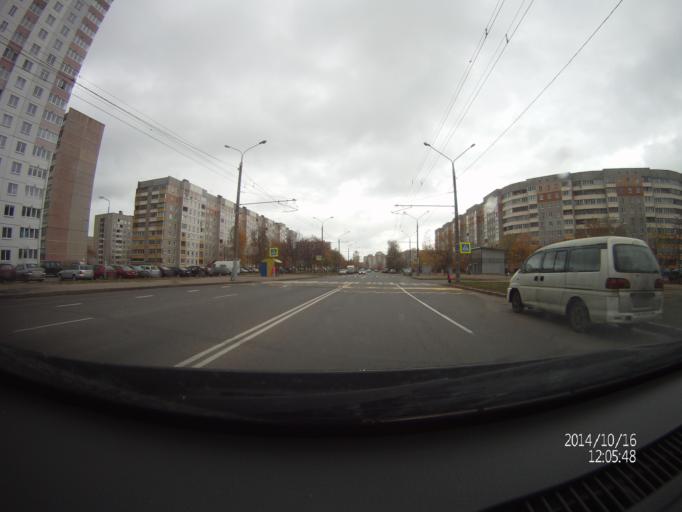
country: BY
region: Minsk
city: Borovlyany
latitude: 53.9357
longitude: 27.6878
